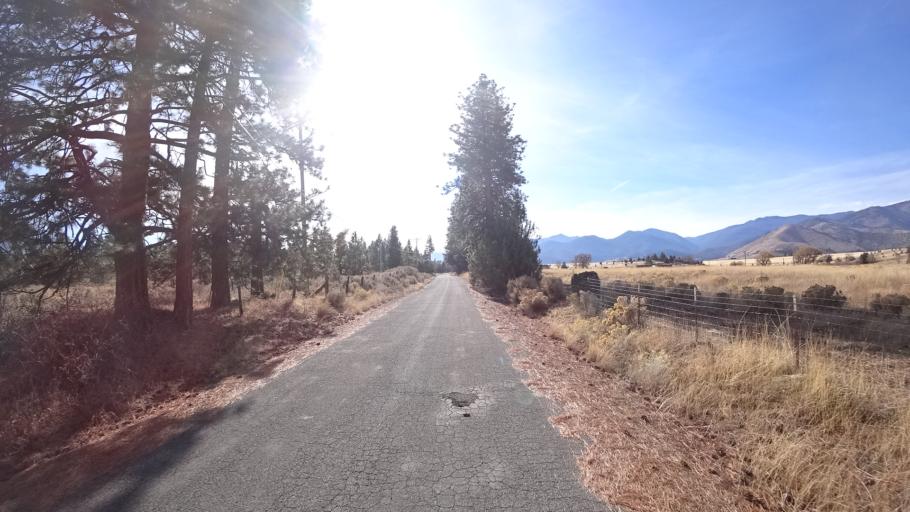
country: US
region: California
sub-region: Siskiyou County
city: Weed
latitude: 41.4856
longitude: -122.4433
